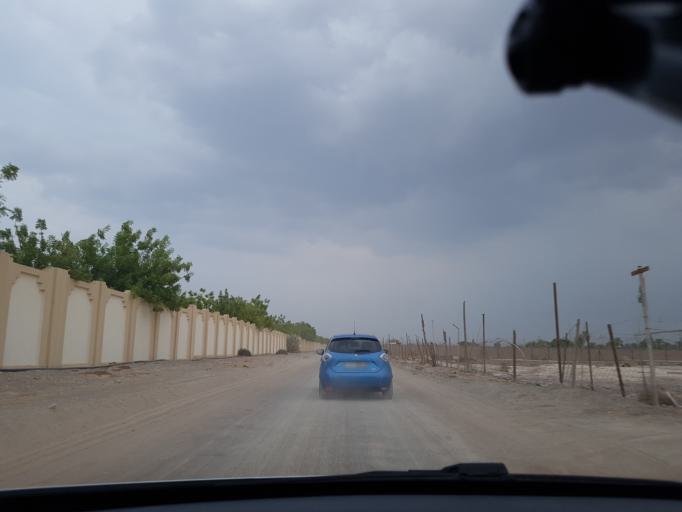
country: AE
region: Ash Shariqah
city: Adh Dhayd
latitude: 25.2752
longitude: 55.9174
